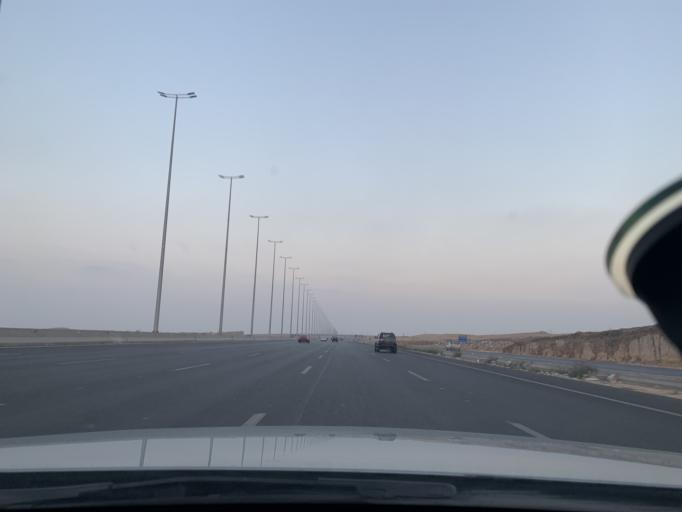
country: EG
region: Muhafazat al Qalyubiyah
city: Al Khankah
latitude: 30.0935
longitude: 31.4931
